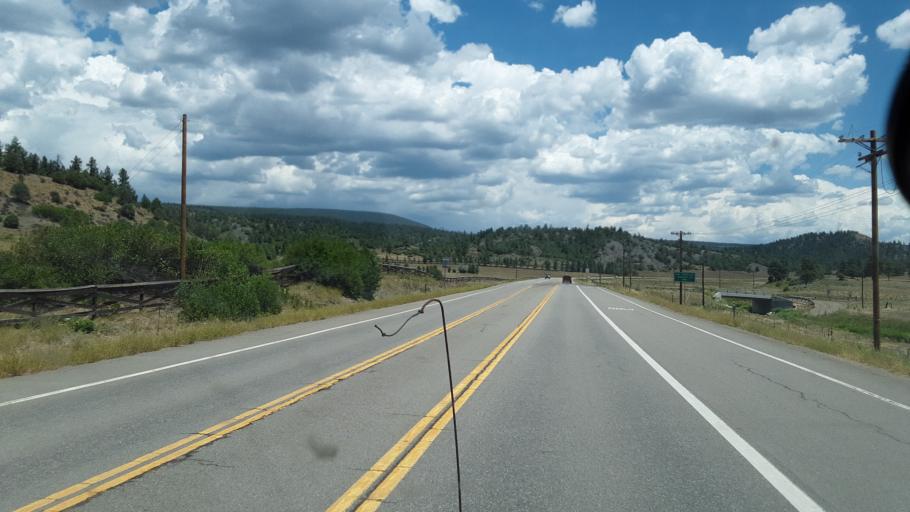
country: US
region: Colorado
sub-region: Archuleta County
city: Pagosa Springs
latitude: 37.2224
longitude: -107.2186
